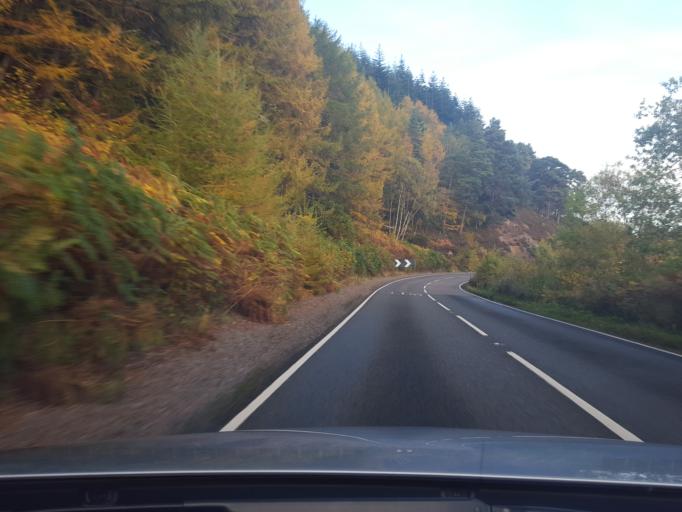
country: GB
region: Scotland
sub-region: Highland
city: Beauly
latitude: 57.3502
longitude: -4.4114
